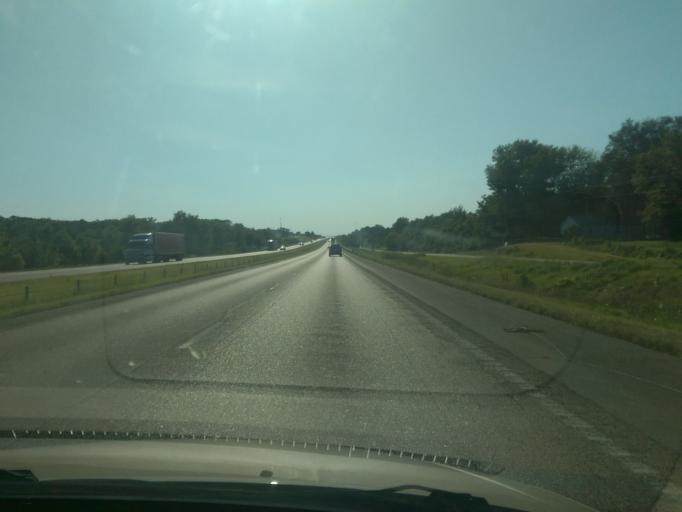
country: US
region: Missouri
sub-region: Lafayette County
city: Odessa
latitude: 39.0049
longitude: -93.8642
